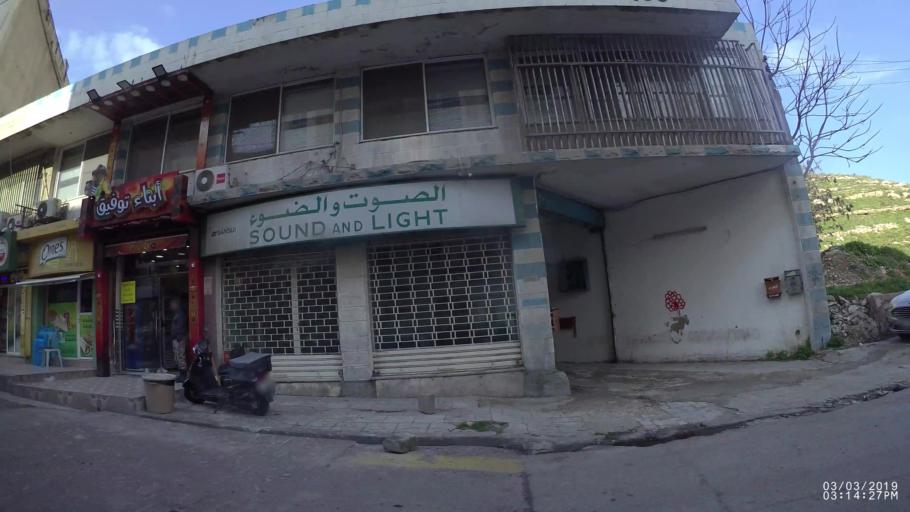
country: JO
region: Amman
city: Amman
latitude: 31.9589
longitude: 35.9075
